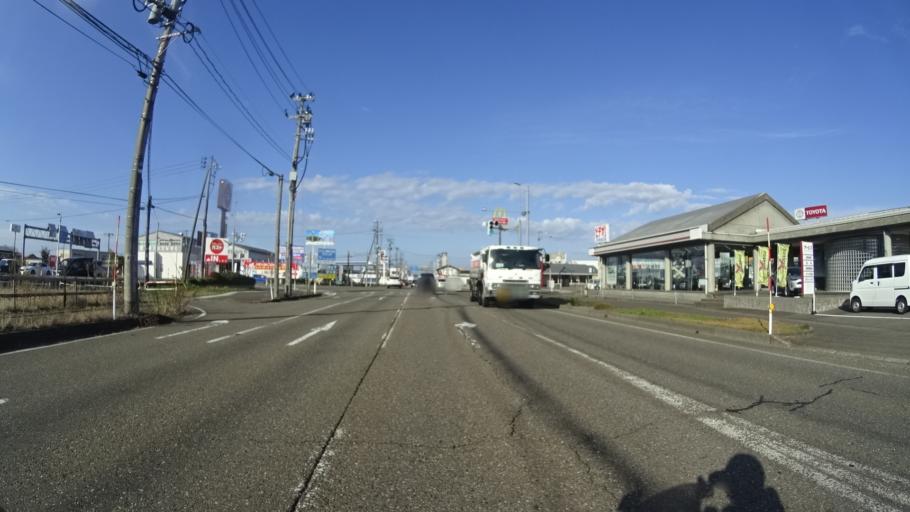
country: JP
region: Niigata
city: Joetsu
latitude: 37.1607
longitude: 138.2375
